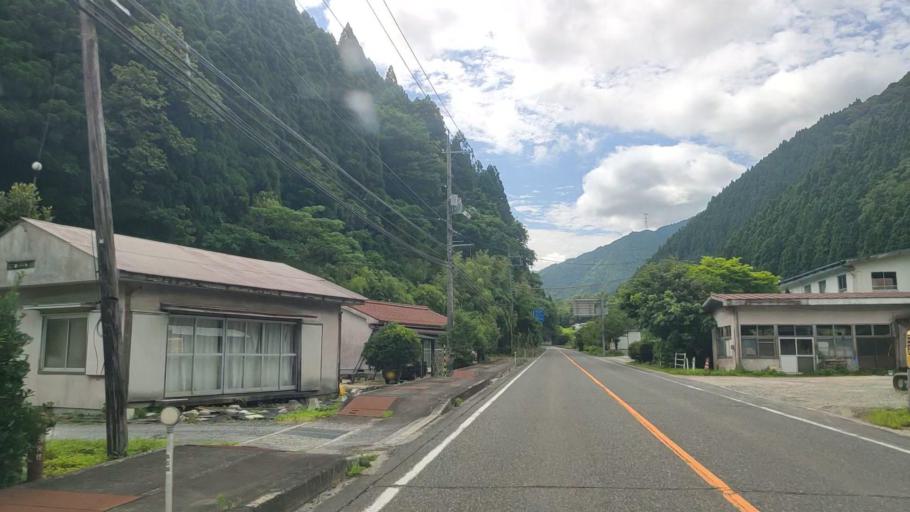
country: JP
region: Tottori
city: Yonago
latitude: 35.2270
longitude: 133.4453
